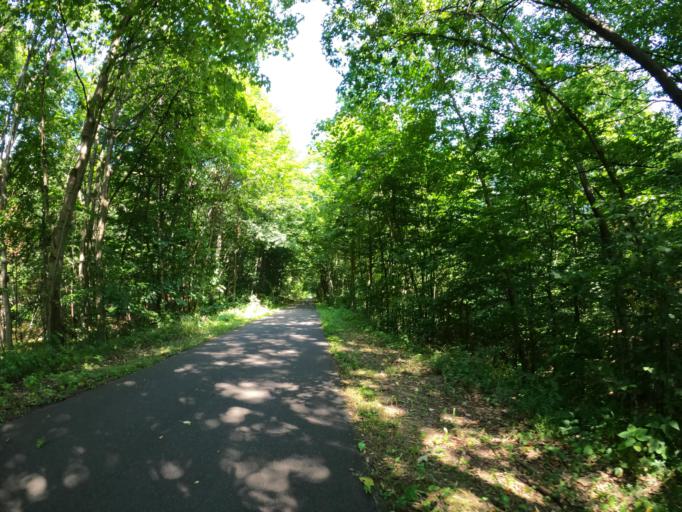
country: DE
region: Brandenburg
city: Templin
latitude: 53.2350
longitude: 13.5024
